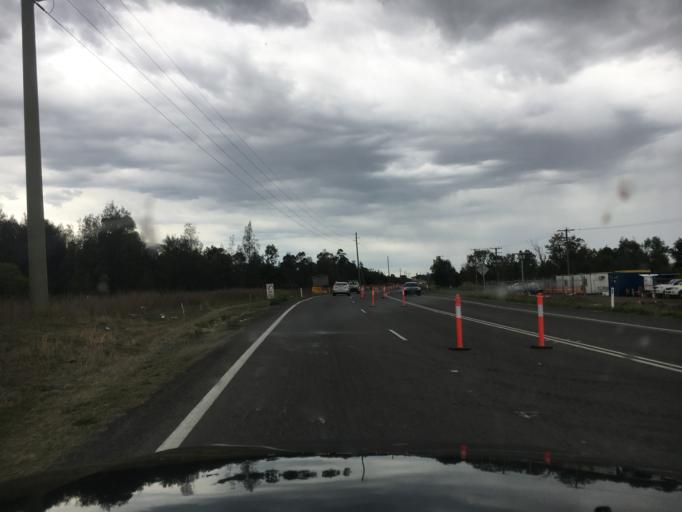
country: AU
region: New South Wales
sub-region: Muswellbrook
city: Muswellbrook
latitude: -32.1907
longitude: 150.8926
